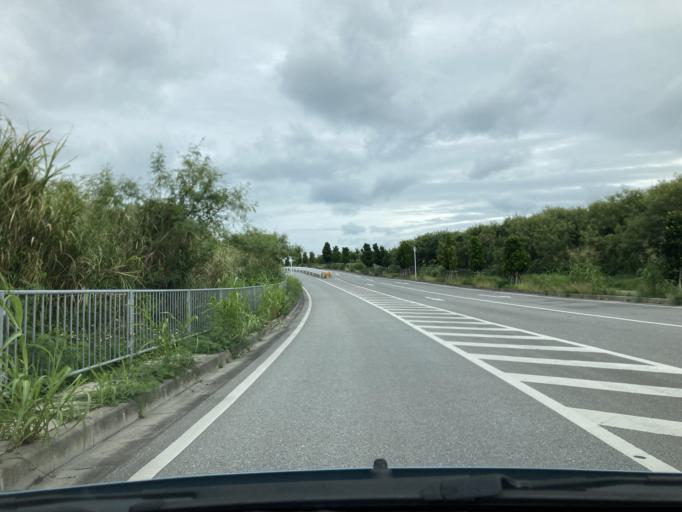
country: JP
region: Okinawa
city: Ginowan
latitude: 26.2112
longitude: 127.7648
